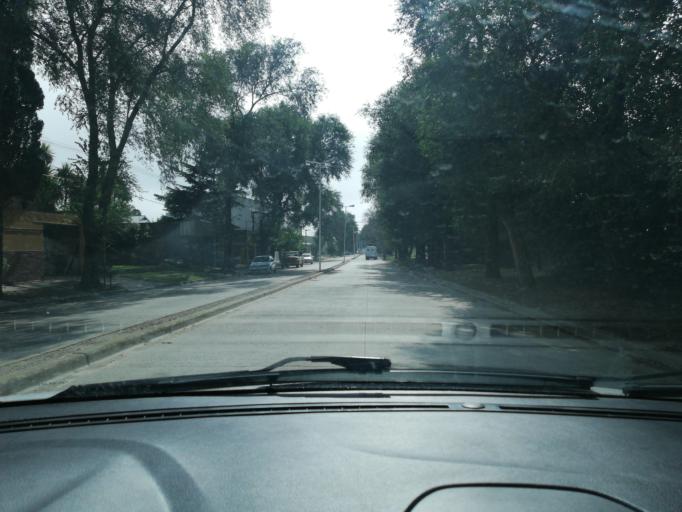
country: AR
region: Buenos Aires
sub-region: Partido de Balcarce
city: Balcarce
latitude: -37.8552
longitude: -58.2436
